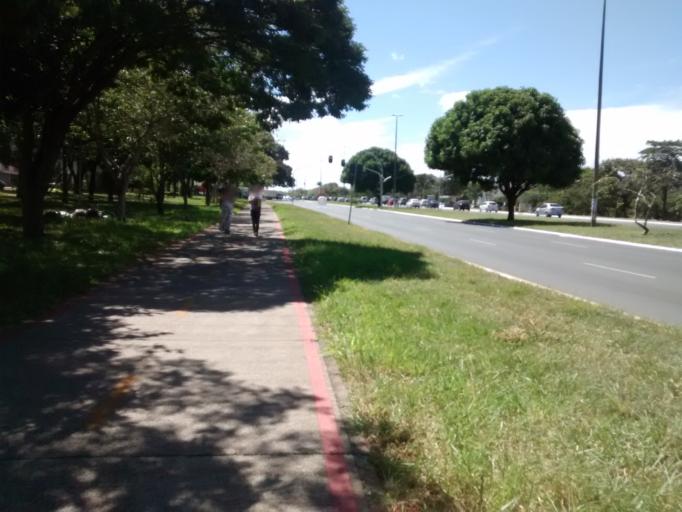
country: BR
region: Federal District
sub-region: Brasilia
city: Brasilia
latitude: -15.8170
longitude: -47.8909
